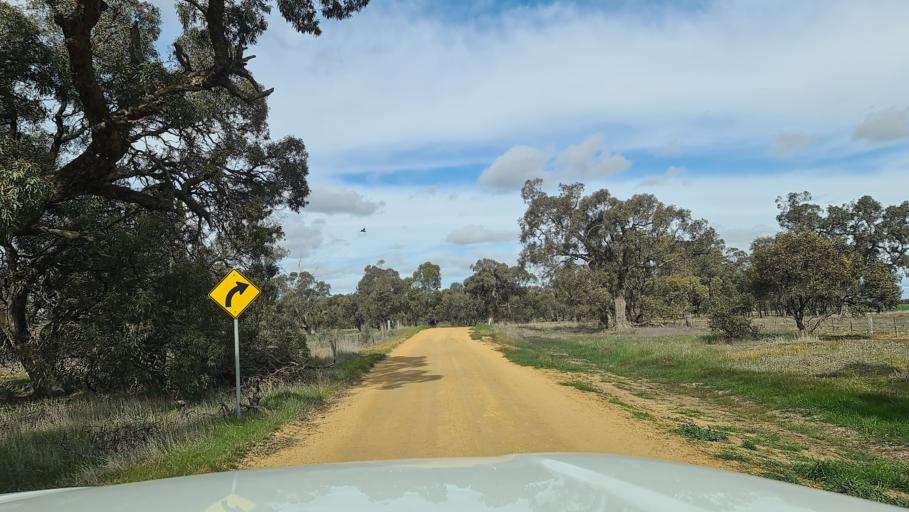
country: AU
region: Victoria
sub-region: Horsham
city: Horsham
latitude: -36.6349
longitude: 142.4118
